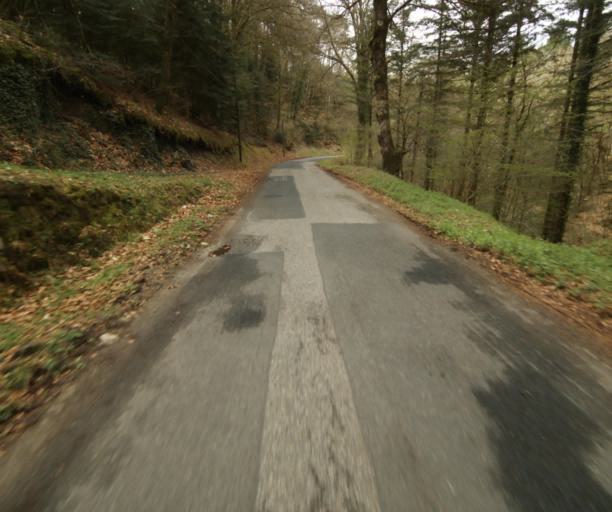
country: FR
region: Limousin
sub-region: Departement de la Correze
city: Argentat
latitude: 45.2028
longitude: 1.9627
